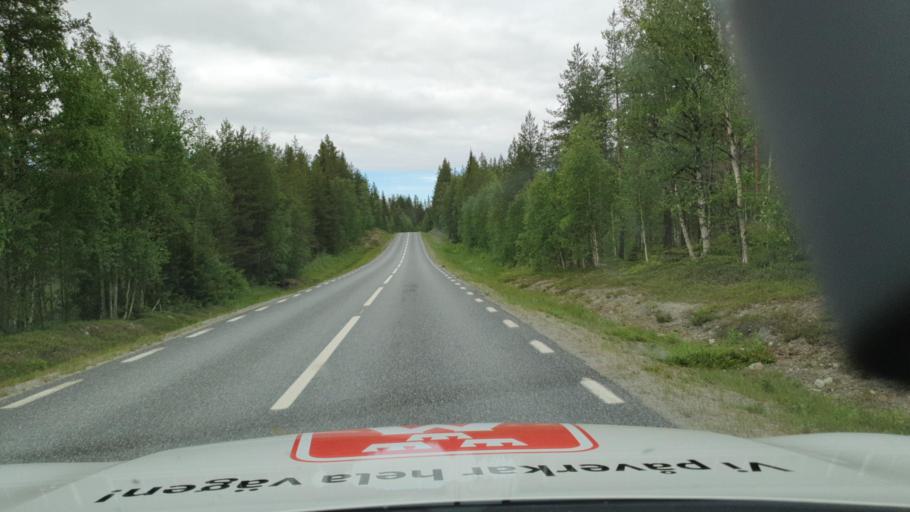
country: SE
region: Vaesterbotten
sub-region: Asele Kommun
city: Insjon
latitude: 64.2403
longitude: 17.5483
